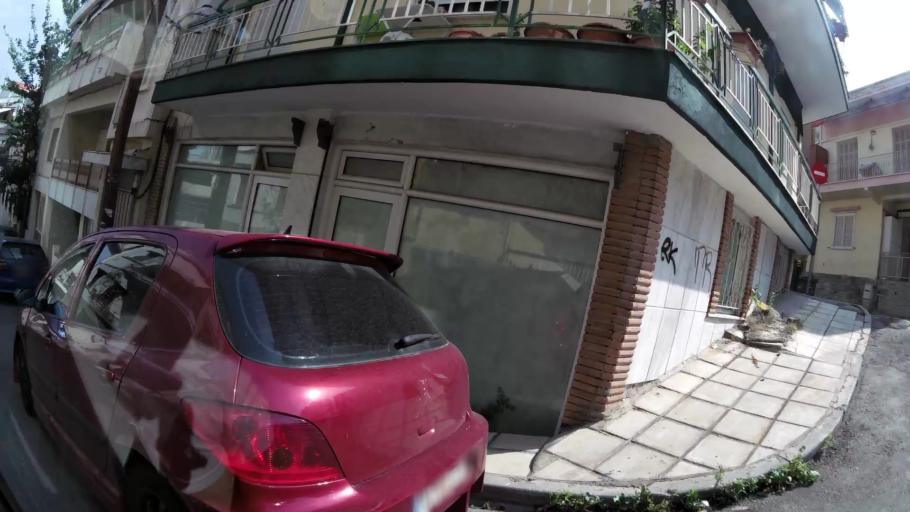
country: GR
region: Central Macedonia
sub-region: Nomos Thessalonikis
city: Sykies
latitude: 40.6483
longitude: 22.9503
